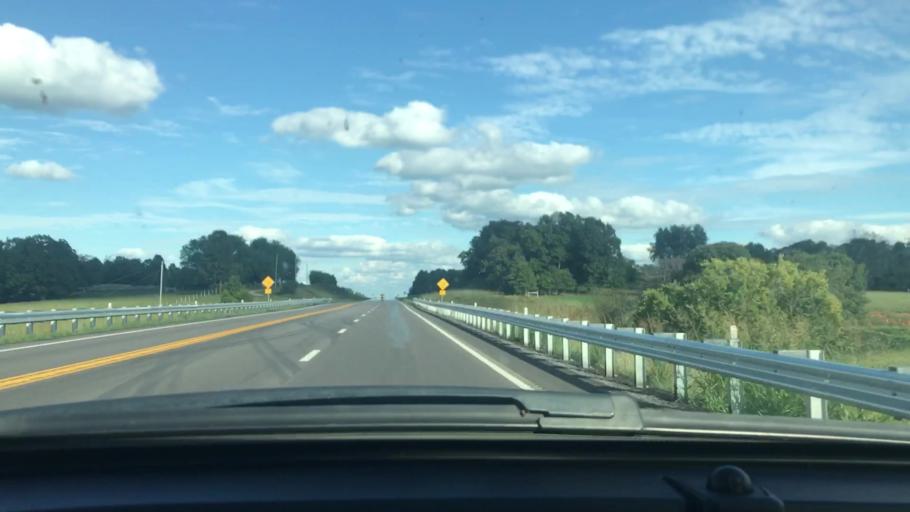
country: US
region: Missouri
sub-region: Oregon County
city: Thayer
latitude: 36.5844
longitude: -91.6169
